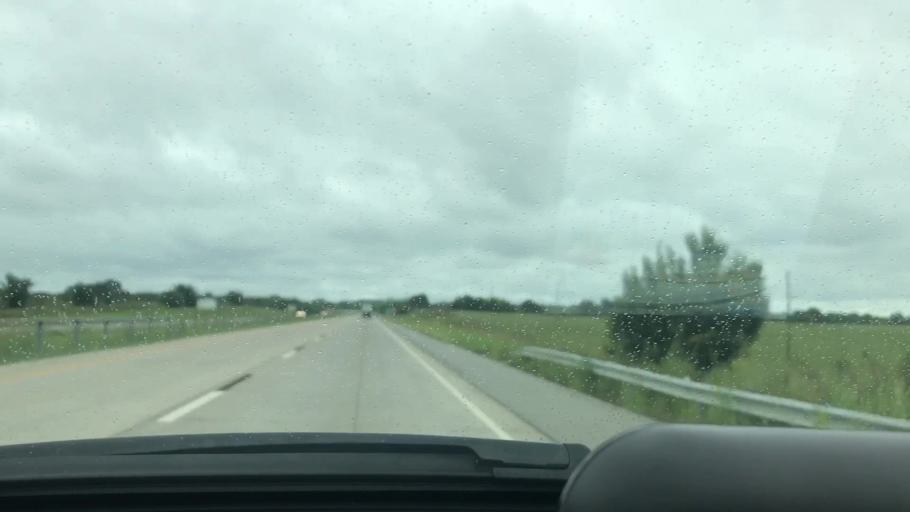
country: US
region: Oklahoma
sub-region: Pittsburg County
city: McAlester
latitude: 34.8140
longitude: -95.8569
